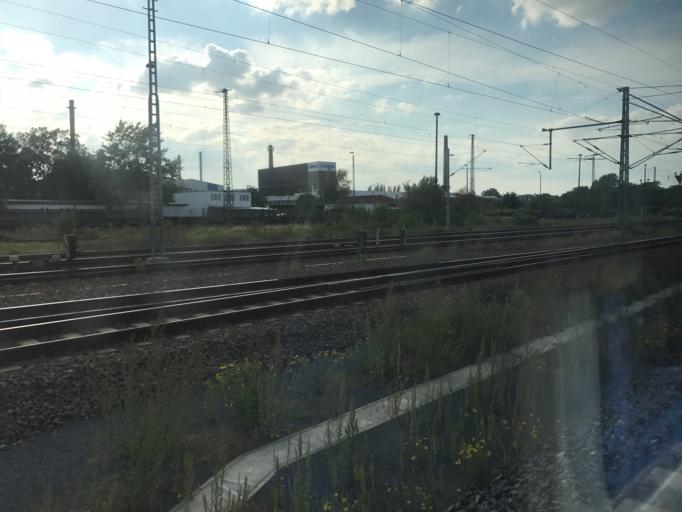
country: DE
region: Saxony
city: Coswig
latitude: 51.1200
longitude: 13.5875
